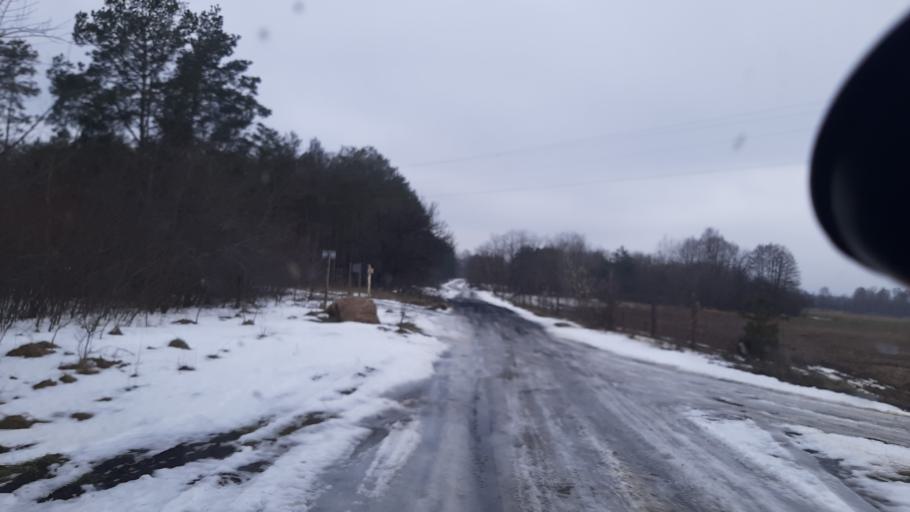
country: PL
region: Lublin Voivodeship
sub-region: Powiat wlodawski
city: Wlodawa
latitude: 51.5168
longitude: 23.5979
